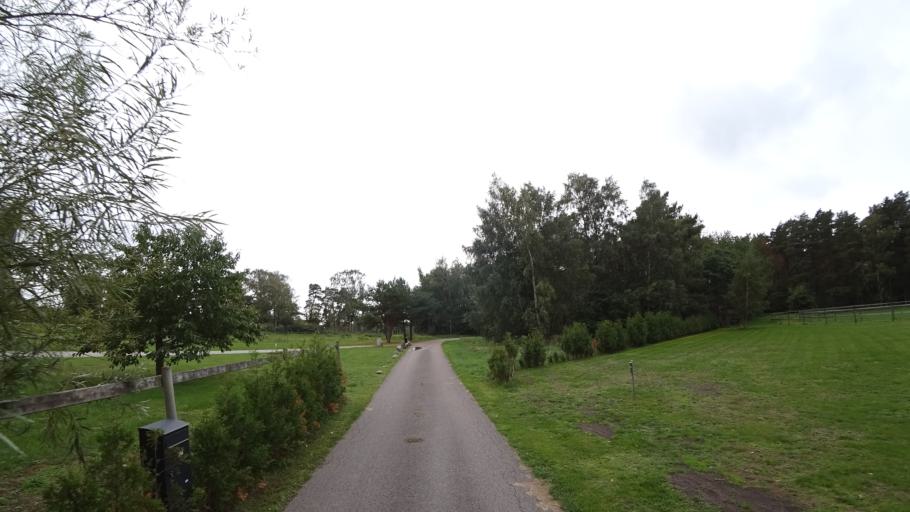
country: SE
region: Skane
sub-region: Kavlinge Kommun
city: Hofterup
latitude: 55.8011
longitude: 12.9946
